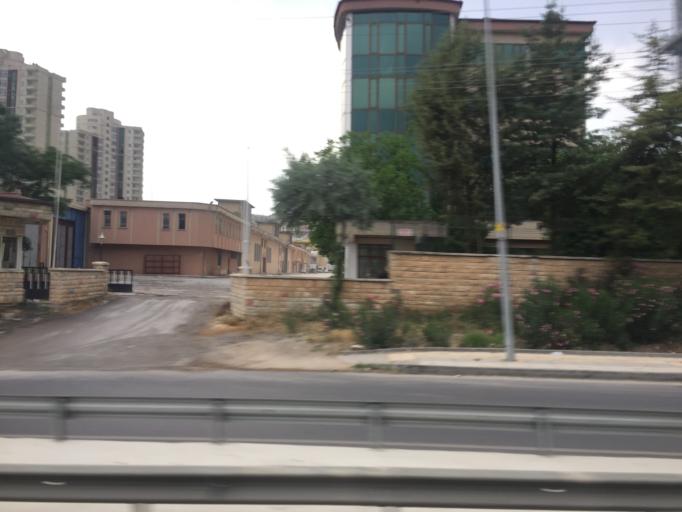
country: TR
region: Gaziantep
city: Gaziantep
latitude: 37.0396
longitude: 37.4238
